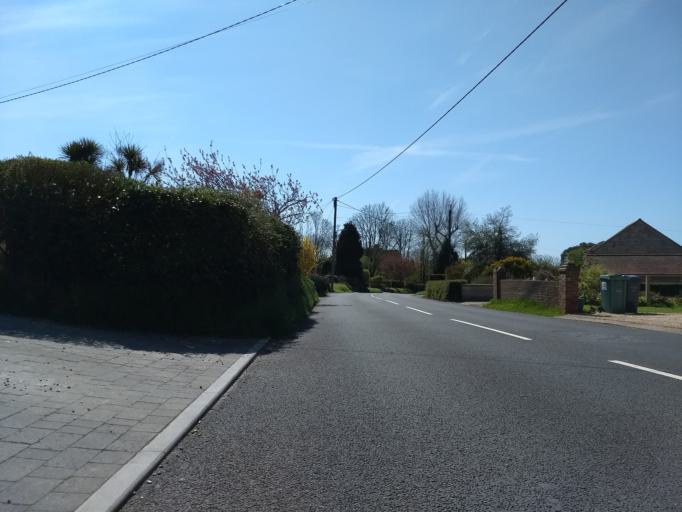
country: GB
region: England
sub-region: Isle of Wight
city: Northwood
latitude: 50.7419
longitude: -1.3193
